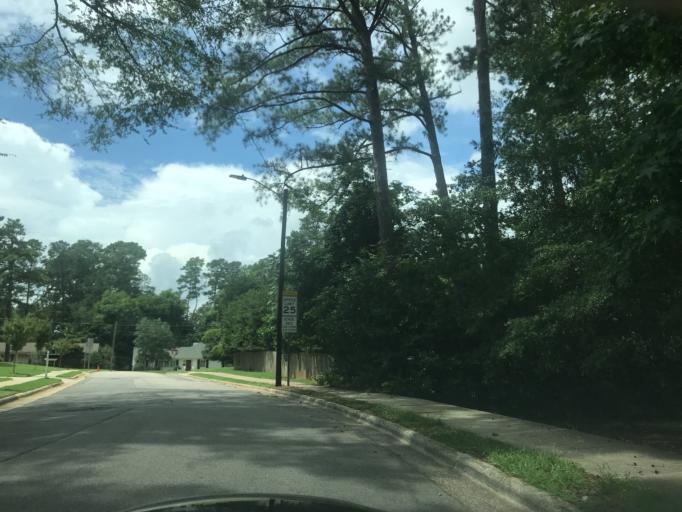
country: US
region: North Carolina
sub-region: Wake County
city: West Raleigh
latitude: 35.8146
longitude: -78.6342
